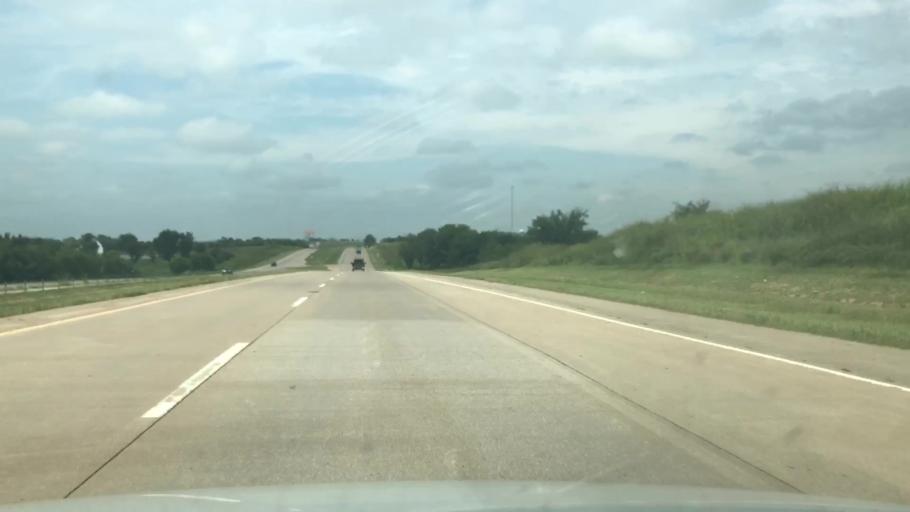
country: US
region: Oklahoma
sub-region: Washington County
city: Bartlesville
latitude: 36.5877
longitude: -95.9320
